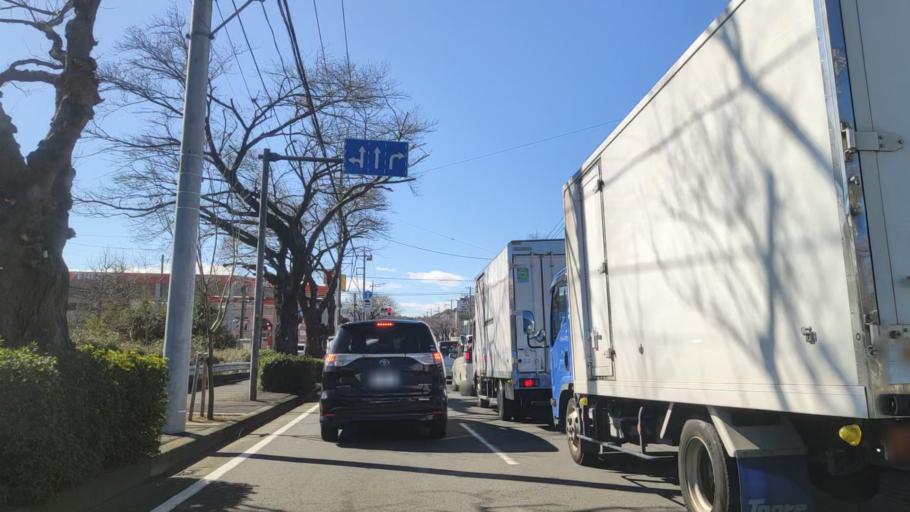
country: JP
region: Tokyo
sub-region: Machida-shi
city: Machida
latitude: 35.5205
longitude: 139.5074
